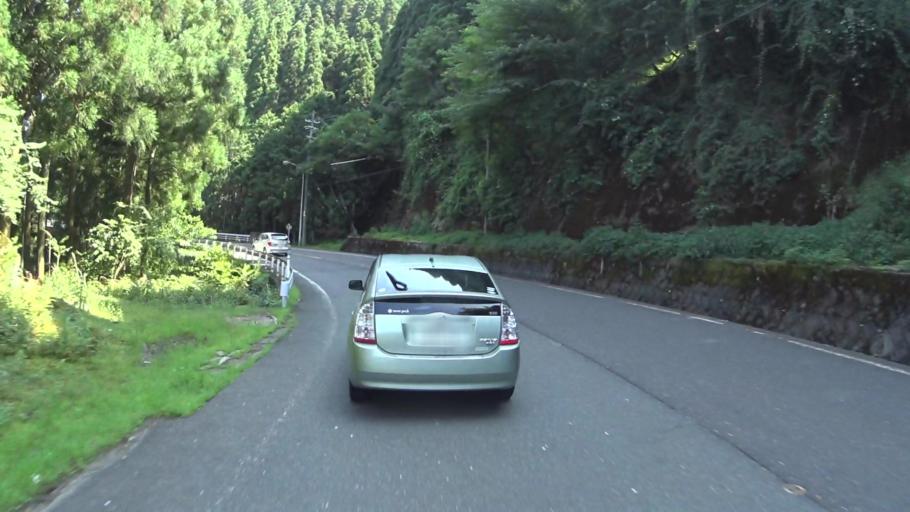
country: JP
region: Fukui
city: Obama
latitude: 35.3872
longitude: 135.5876
